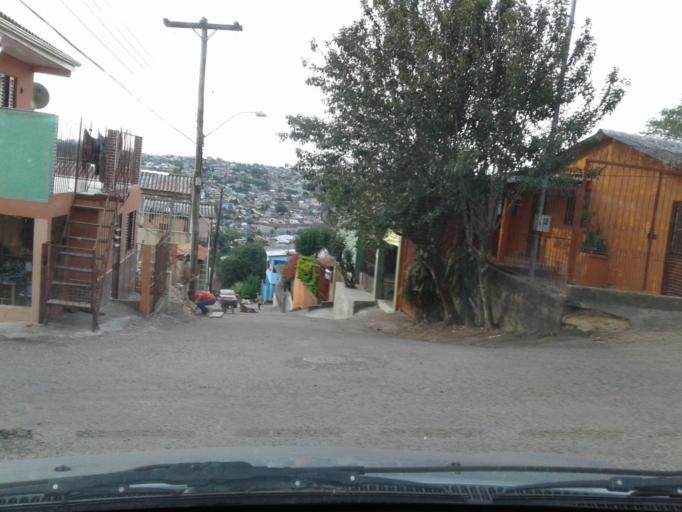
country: BR
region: Rio Grande do Sul
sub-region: Porto Alegre
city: Porto Alegre
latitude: -30.0617
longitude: -51.1441
